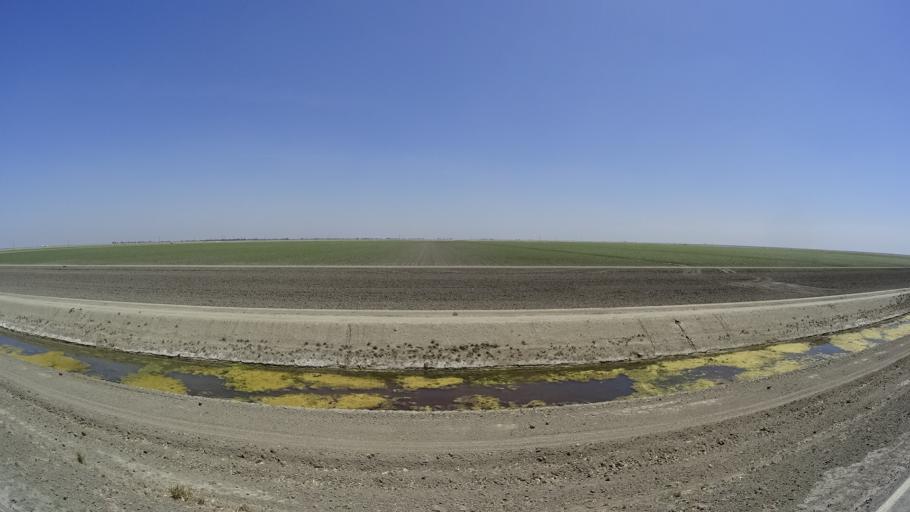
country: US
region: California
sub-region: Kings County
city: Corcoran
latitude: 36.0758
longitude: -119.6439
